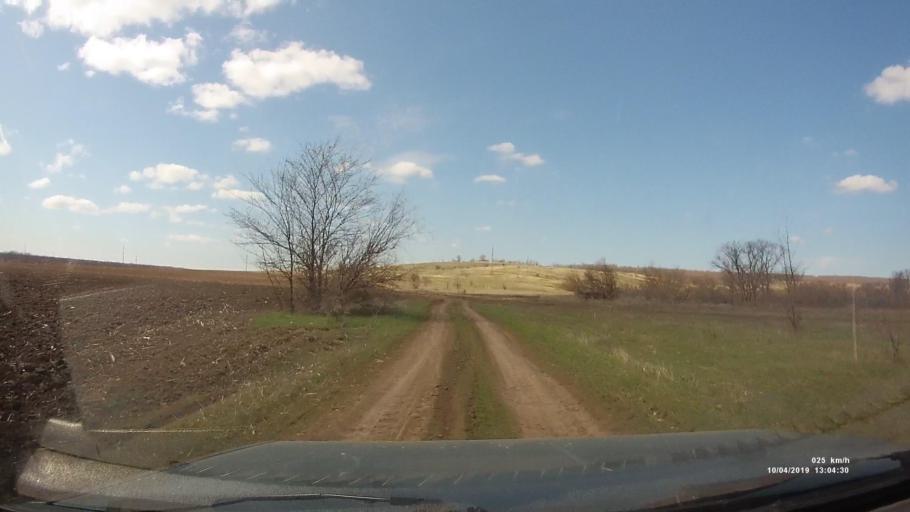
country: RU
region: Rostov
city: Masalovka
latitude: 48.3855
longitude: 40.2360
